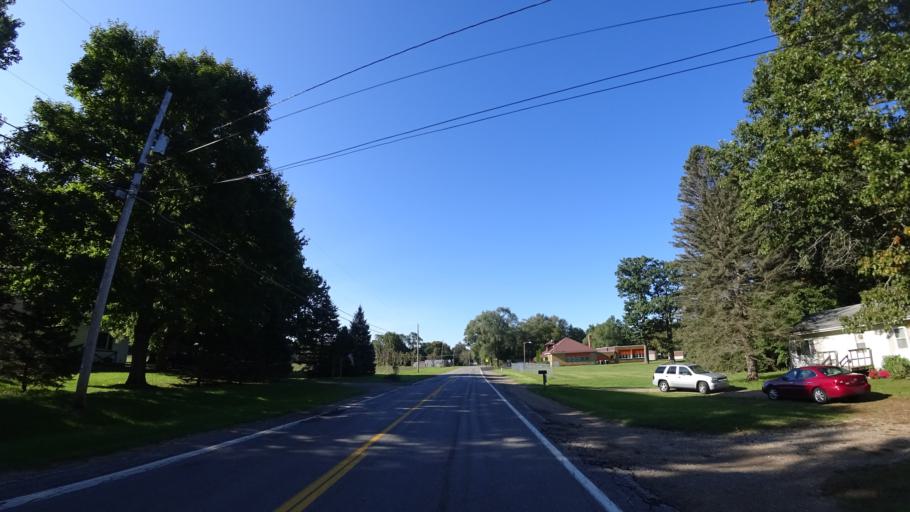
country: US
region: Michigan
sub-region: Berrien County
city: Benton Heights
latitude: 42.1743
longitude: -86.3869
